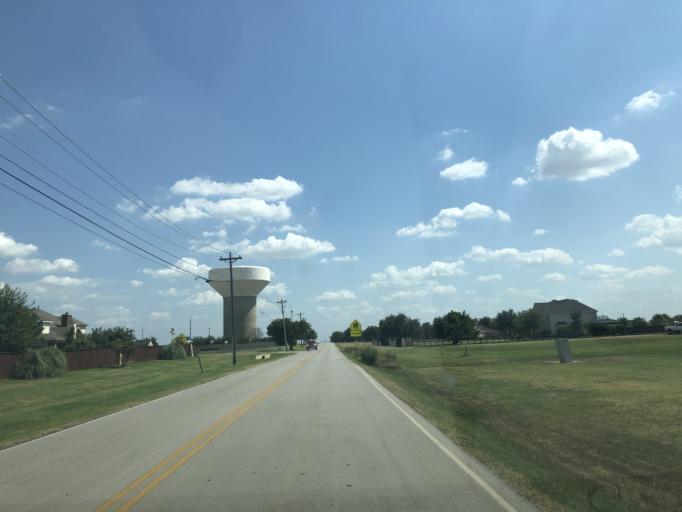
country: US
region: Texas
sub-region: Tarrant County
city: Haslet
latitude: 32.9306
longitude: -97.3316
